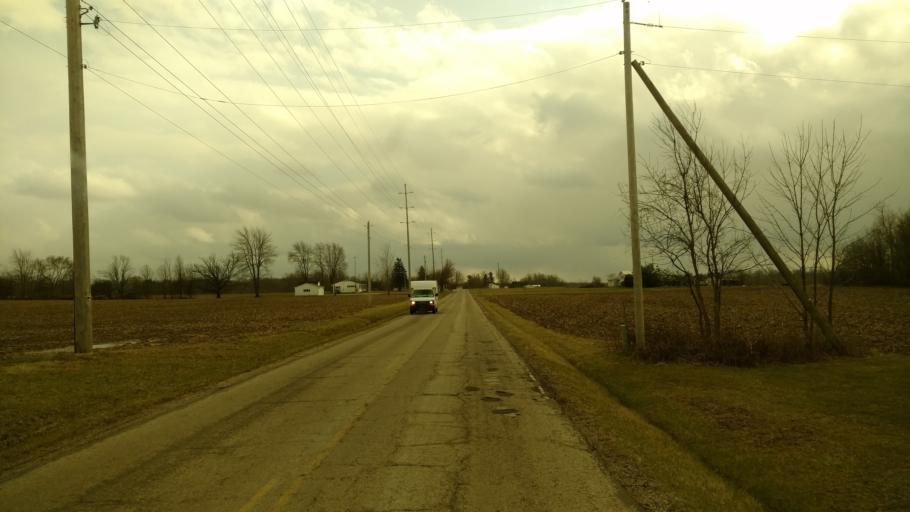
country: US
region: Ohio
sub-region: Crawford County
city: Crestline
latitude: 40.7772
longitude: -82.6979
